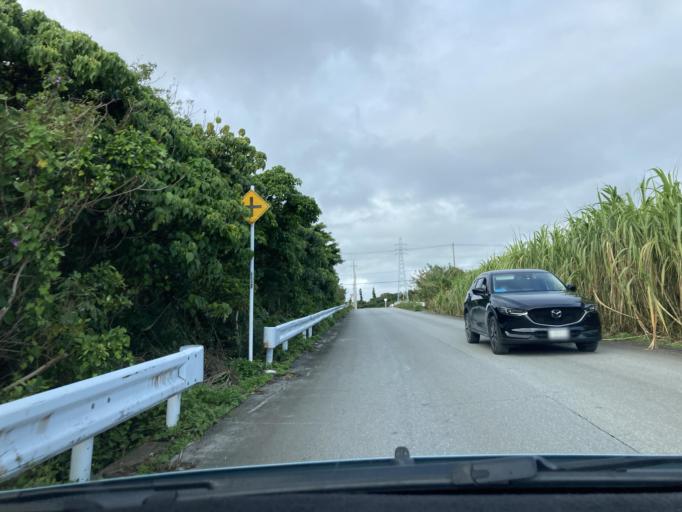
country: JP
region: Okinawa
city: Itoman
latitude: 26.1186
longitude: 127.6851
